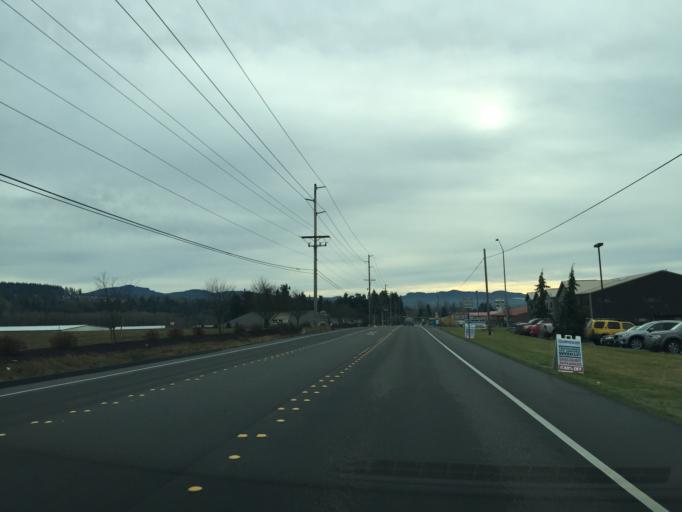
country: US
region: Washington
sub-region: Whatcom County
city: Bellingham
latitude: 48.7930
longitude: -122.4427
